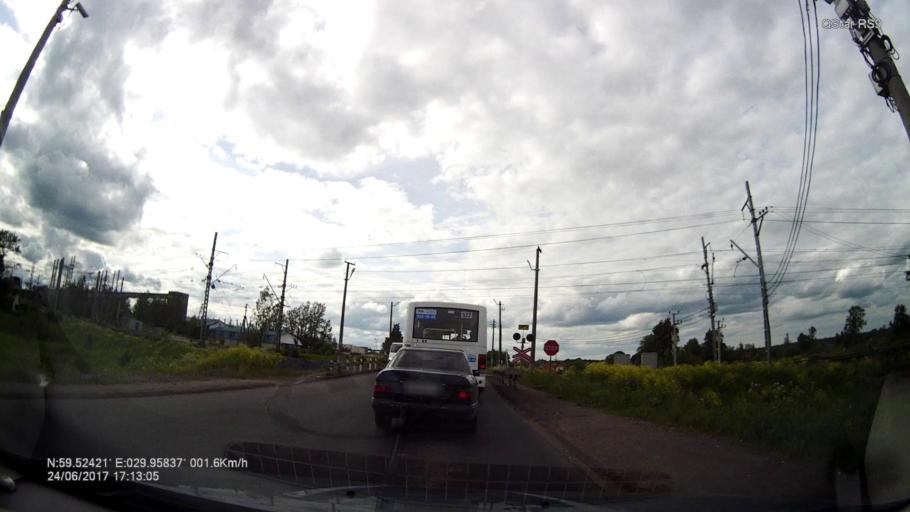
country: RU
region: Leningrad
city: Voyskovitsy
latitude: 59.5242
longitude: 29.9583
